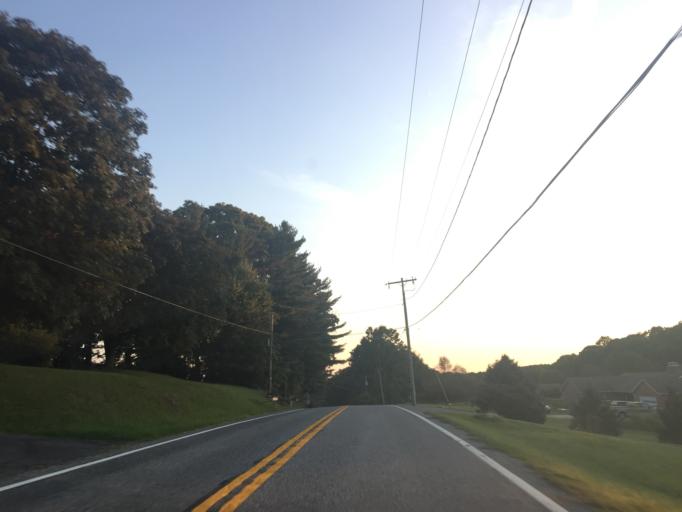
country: US
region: Pennsylvania
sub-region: York County
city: Susquehanna Trails
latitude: 39.6768
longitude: -76.3137
